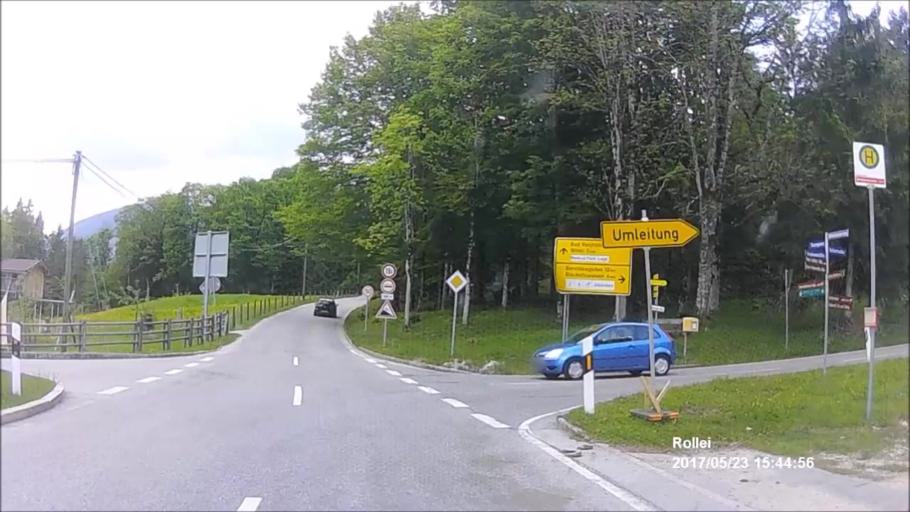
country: DE
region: Bavaria
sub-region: Upper Bavaria
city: Bischofswiesen
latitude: 47.6521
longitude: 12.9323
